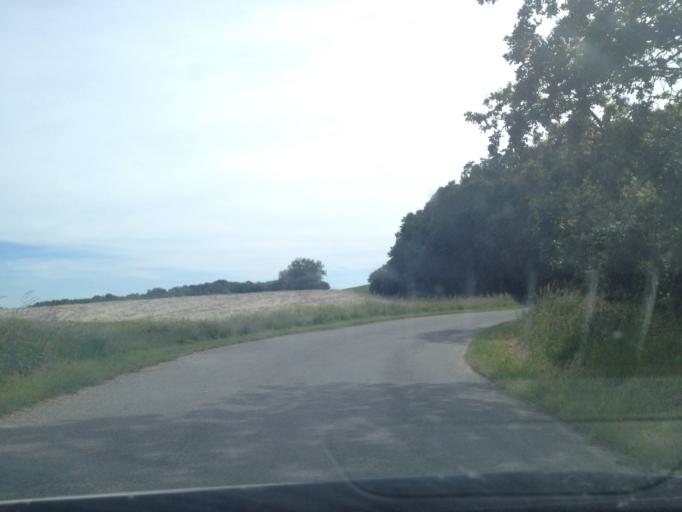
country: DK
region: Central Jutland
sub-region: Samso Kommune
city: Tranebjerg
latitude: 55.7762
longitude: 10.5526
